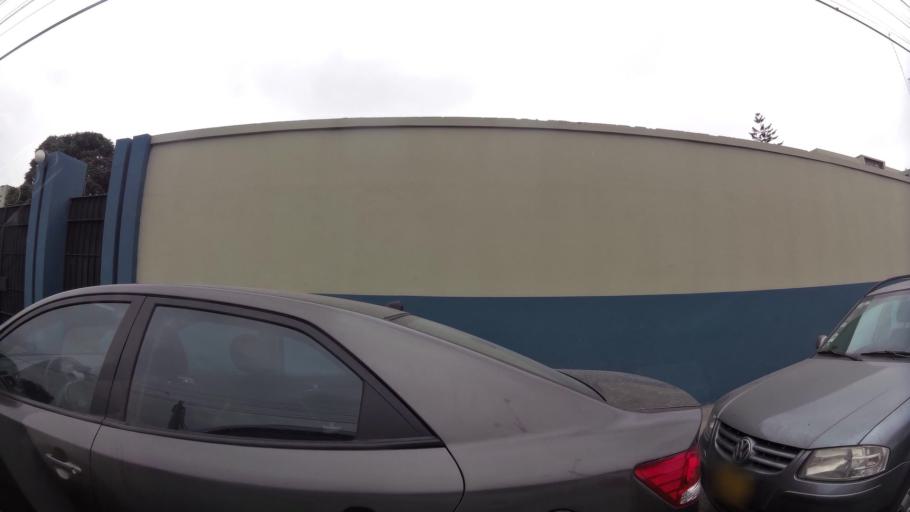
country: PE
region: Lima
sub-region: Lima
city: La Molina
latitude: -12.0943
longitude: -76.9738
